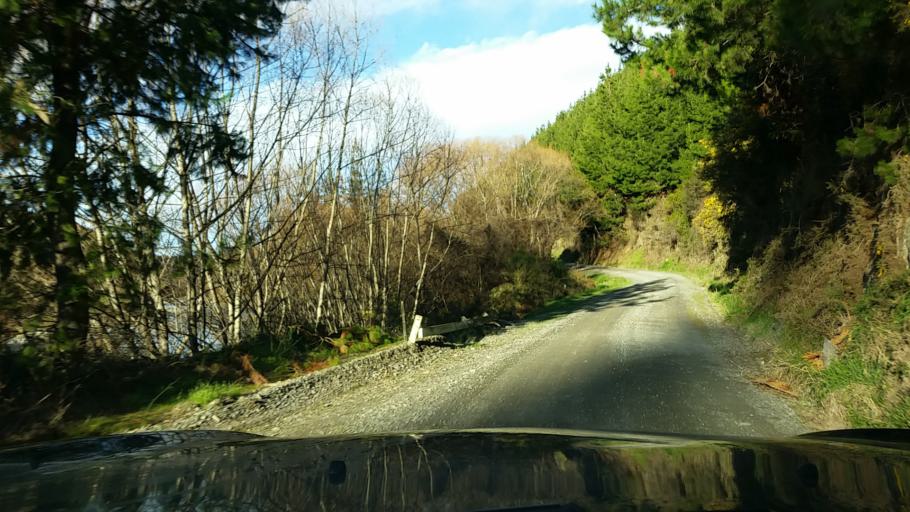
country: NZ
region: Nelson
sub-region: Nelson City
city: Nelson
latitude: -41.5623
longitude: 173.4330
